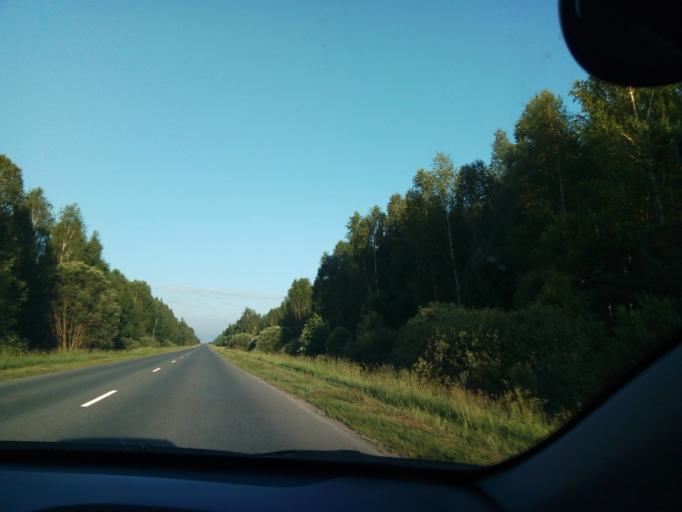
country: RU
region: Nizjnij Novgorod
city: Satis
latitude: 54.8943
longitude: 43.1031
